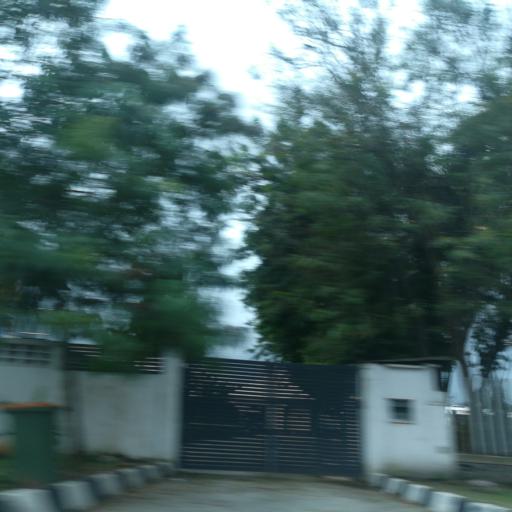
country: NG
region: Lagos
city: Ikoyi
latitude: 6.4559
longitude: 3.4458
